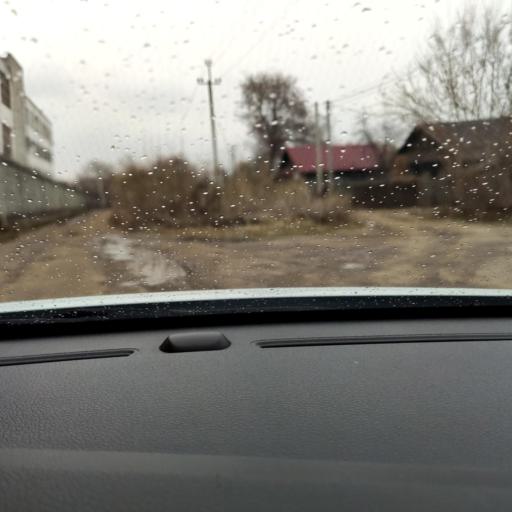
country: RU
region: Tatarstan
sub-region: Gorod Kazan'
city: Kazan
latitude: 55.7532
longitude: 49.1356
